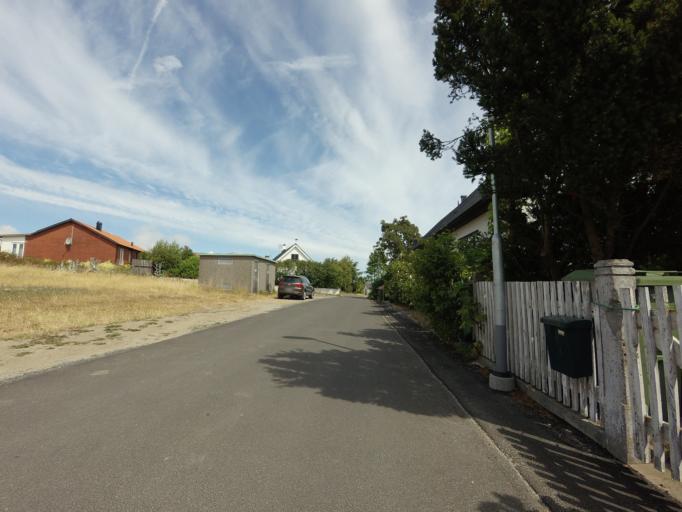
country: SE
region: Skane
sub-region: Simrishamns Kommun
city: Simrishamn
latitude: 55.5434
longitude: 14.3570
